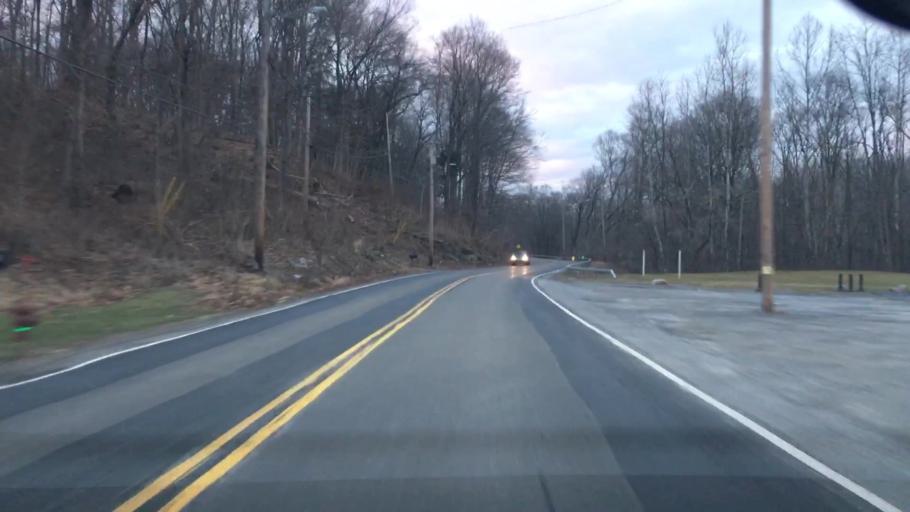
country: US
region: New York
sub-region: Dutchess County
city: Red Oaks Mill
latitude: 41.6640
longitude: -73.8766
